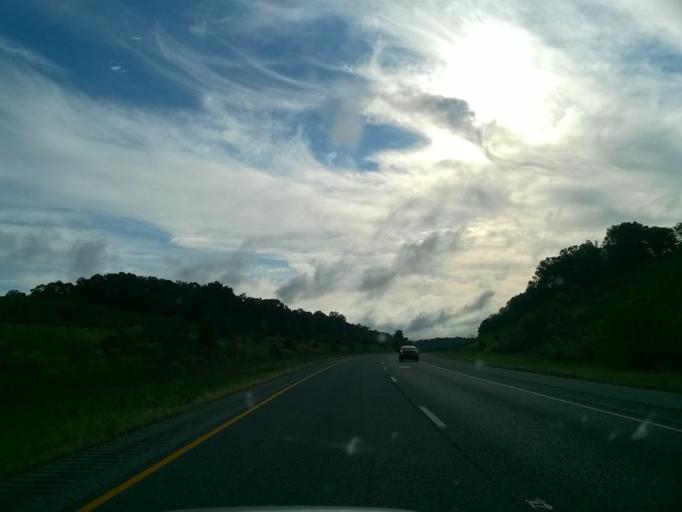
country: US
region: Indiana
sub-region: Dubois County
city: Ferdinand
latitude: 38.2065
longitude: -86.7918
